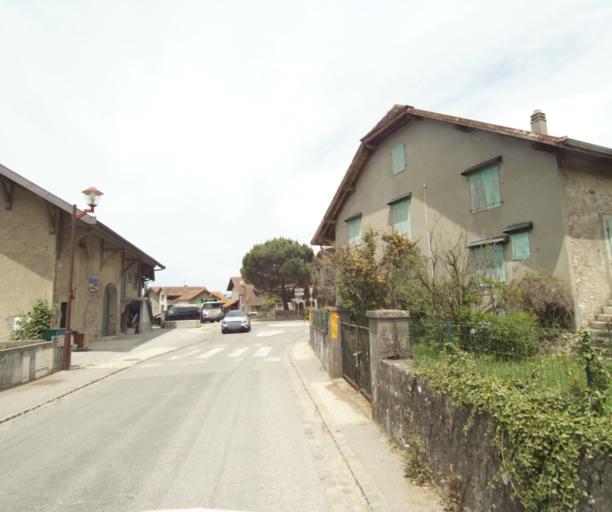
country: FR
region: Rhone-Alpes
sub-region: Departement de la Haute-Savoie
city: Bons-en-Chablais
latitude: 46.2751
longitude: 6.4113
